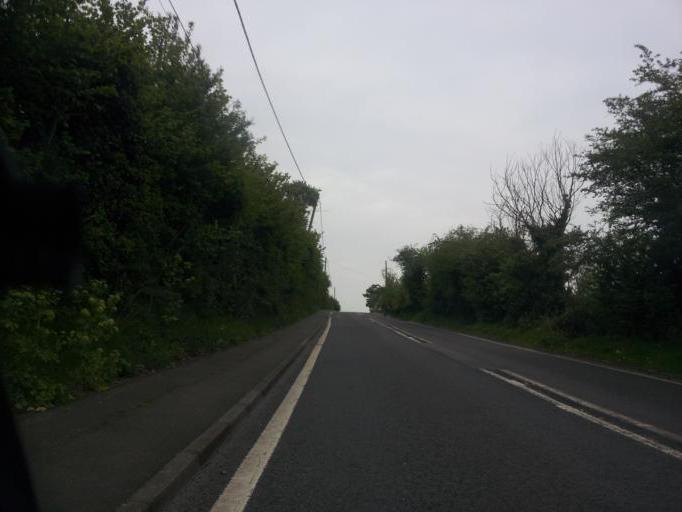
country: GB
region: England
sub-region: Kent
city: Hoo
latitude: 51.4259
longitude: 0.5430
